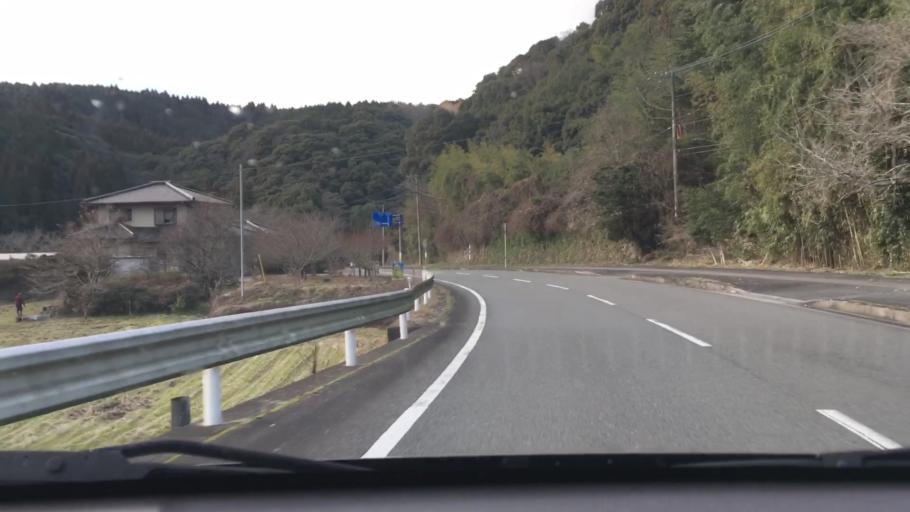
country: JP
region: Oita
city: Hiji
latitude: 33.4223
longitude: 131.4157
